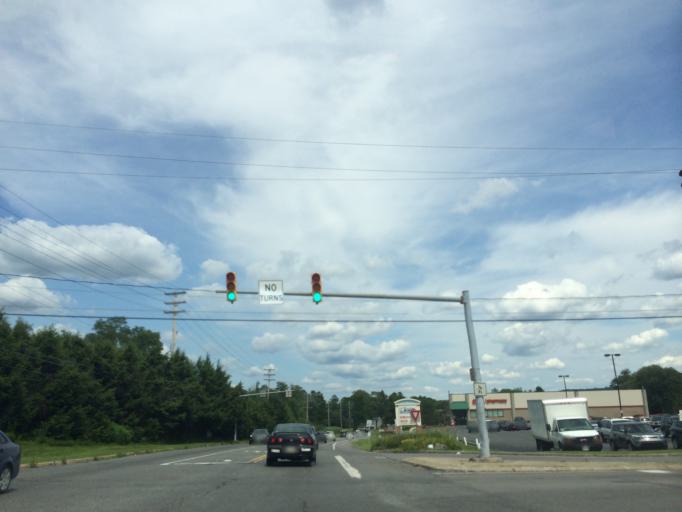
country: US
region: Pennsylvania
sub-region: Pike County
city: Saw Creek
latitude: 41.0626
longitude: -75.0736
